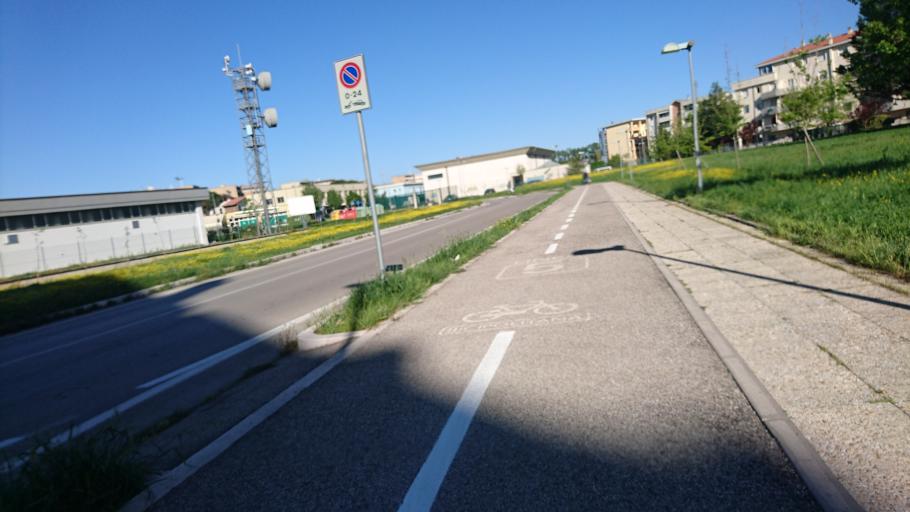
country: IT
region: The Marches
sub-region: Provincia di Pesaro e Urbino
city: Pesaro
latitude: 43.8912
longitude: 12.9015
